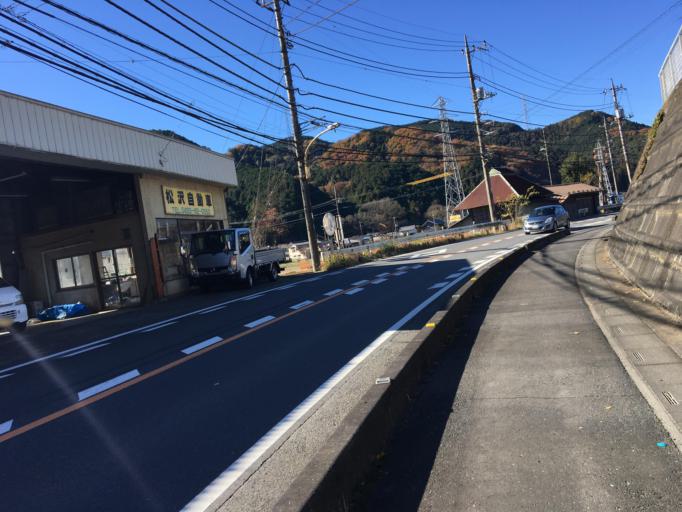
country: JP
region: Saitama
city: Ogawa
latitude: 36.0497
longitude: 139.2128
